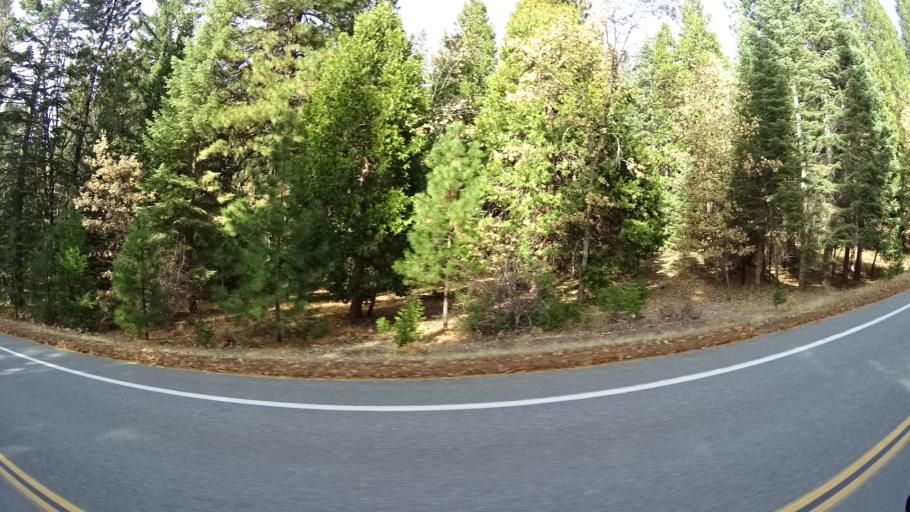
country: US
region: California
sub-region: Siskiyou County
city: Weed
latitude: 41.3818
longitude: -122.3911
